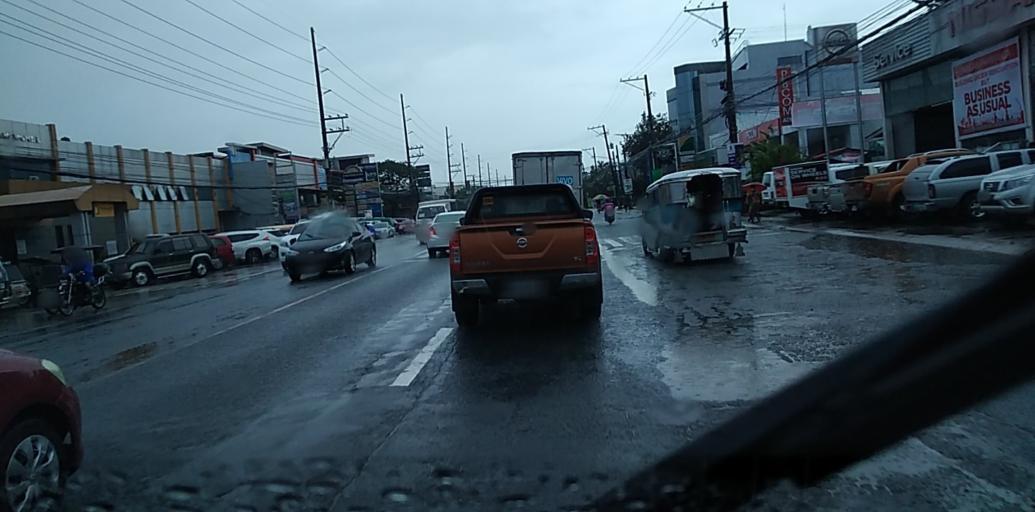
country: PH
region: Central Luzon
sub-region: Province of Pampanga
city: Magliman
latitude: 15.0436
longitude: 120.6744
